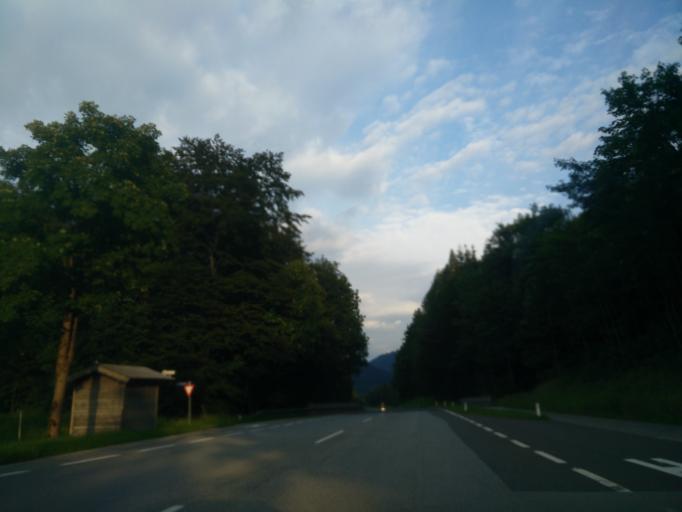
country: AT
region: Salzburg
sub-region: Politischer Bezirk Salzburg-Umgebung
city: Fuschl am See
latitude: 47.7993
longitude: 13.2701
